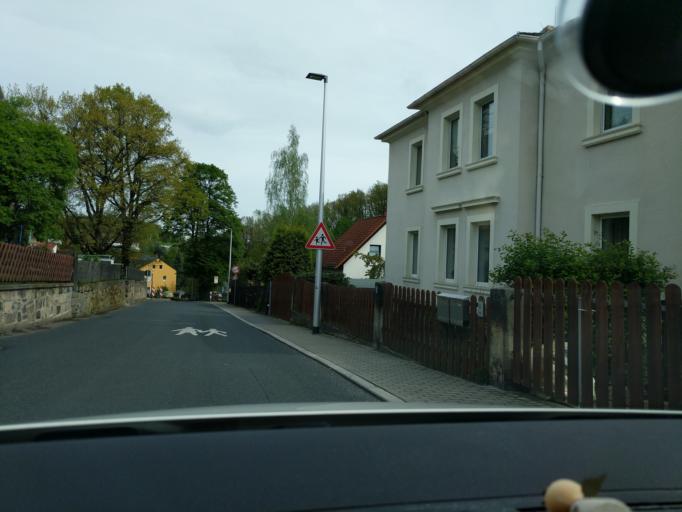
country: DE
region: Saxony
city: Bannewitz
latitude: 50.9954
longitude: 13.6901
